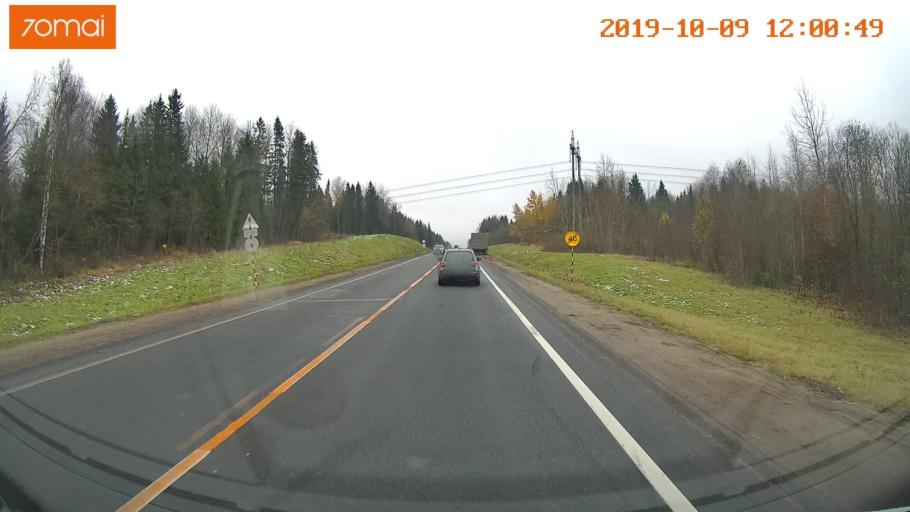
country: RU
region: Vologda
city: Gryazovets
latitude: 58.6941
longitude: 40.3008
